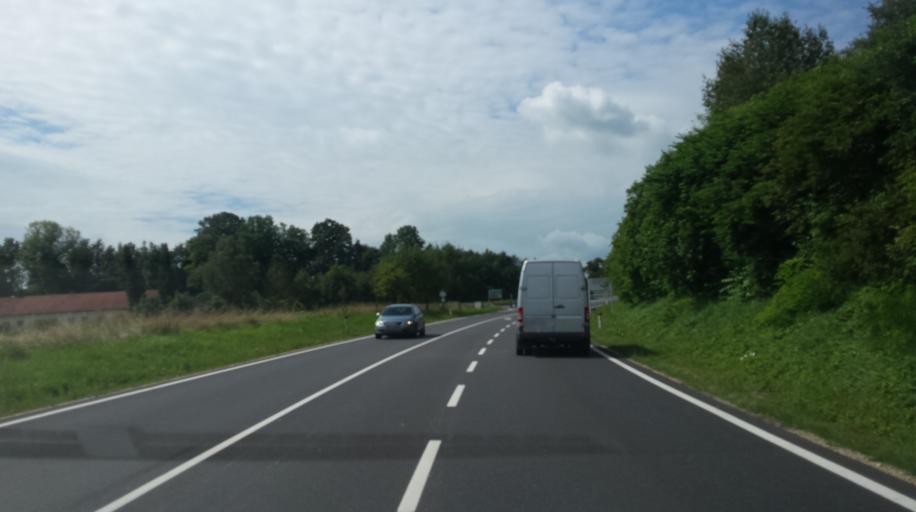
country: AT
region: Lower Austria
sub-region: Politischer Bezirk Amstetten
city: Haag
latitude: 48.1067
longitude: 14.5506
